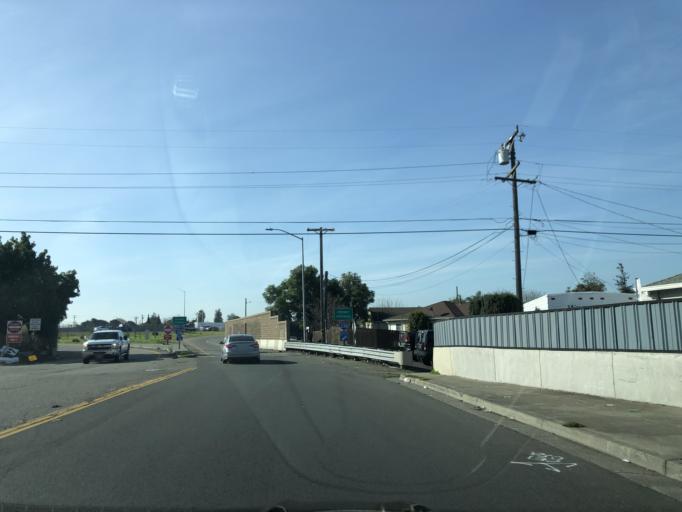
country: US
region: California
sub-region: Alameda County
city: Ashland
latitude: 37.6903
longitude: -122.1076
